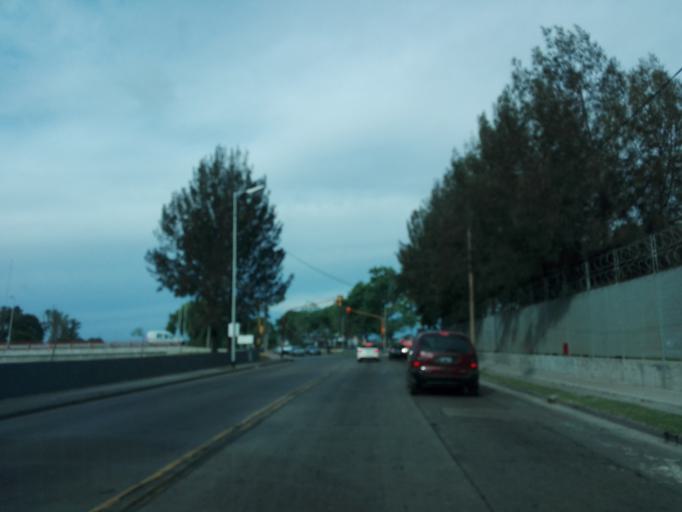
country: AR
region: Buenos Aires
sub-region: Partido de Avellaneda
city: Avellaneda
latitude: -34.6785
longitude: -58.3374
